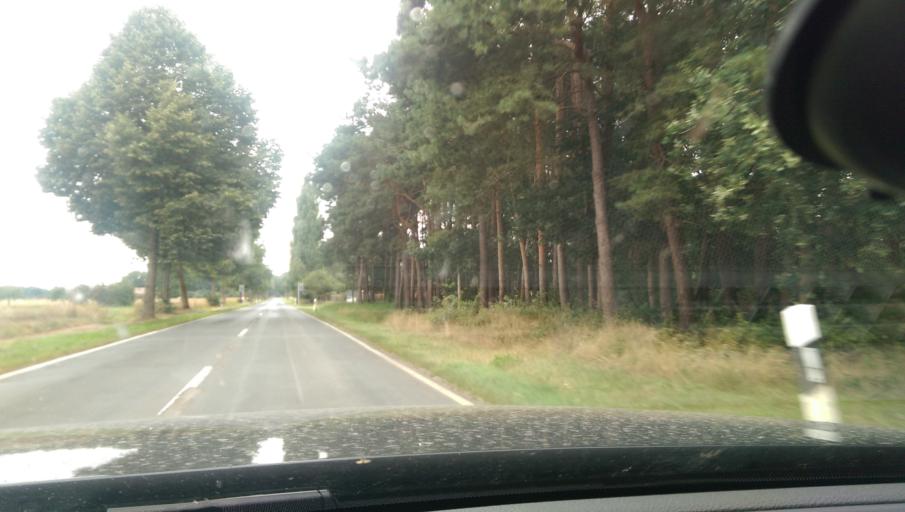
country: DE
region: Lower Saxony
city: Schwarmstedt
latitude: 52.5938
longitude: 9.5957
